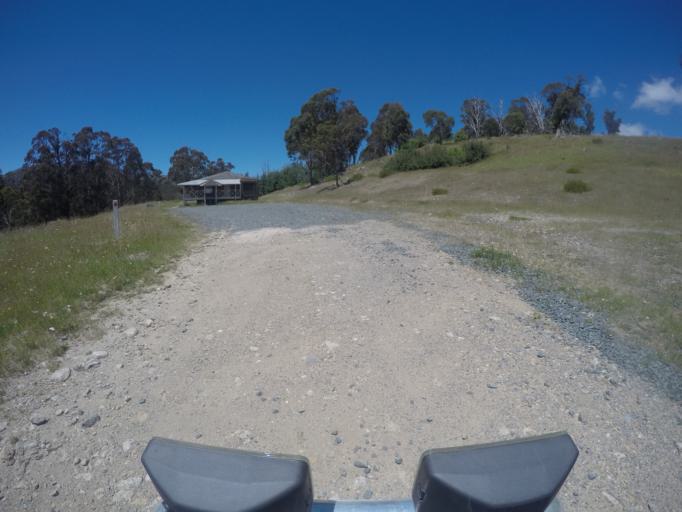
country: AU
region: New South Wales
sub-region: Snowy River
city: Jindabyne
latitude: -35.9374
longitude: 148.3801
